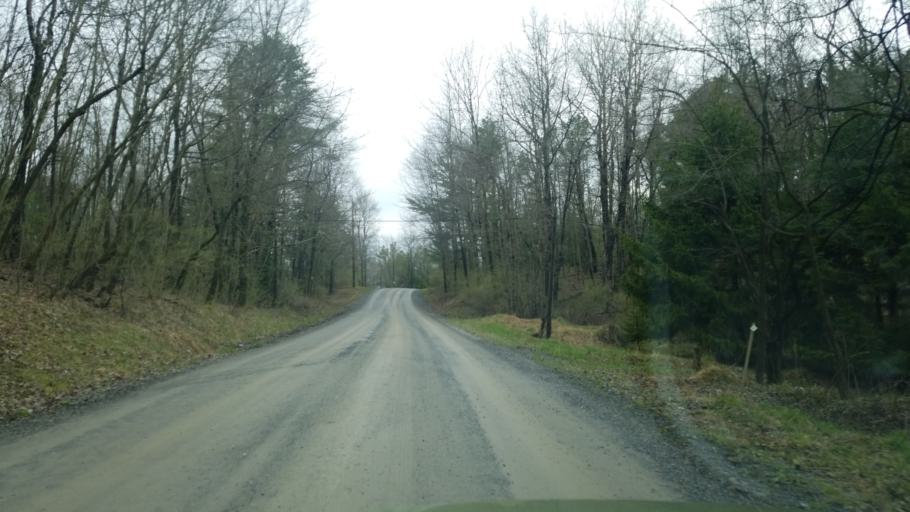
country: US
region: Pennsylvania
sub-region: Clearfield County
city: Shiloh
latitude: 41.1321
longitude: -78.3344
